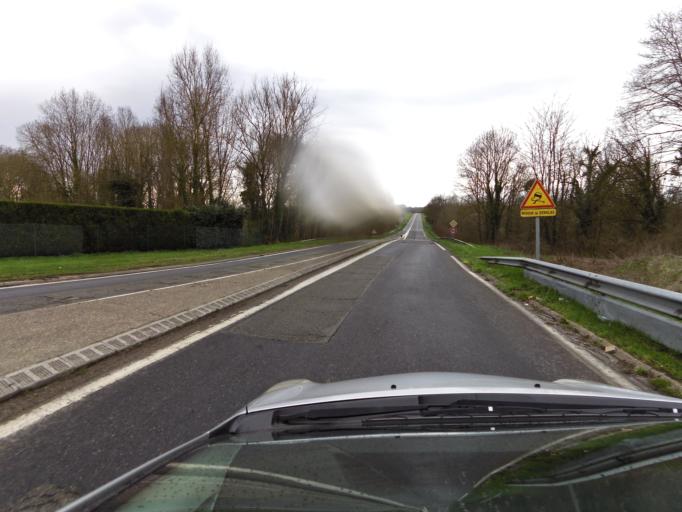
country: FR
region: Picardie
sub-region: Departement de l'Oise
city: Chamant
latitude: 49.1934
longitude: 2.6396
